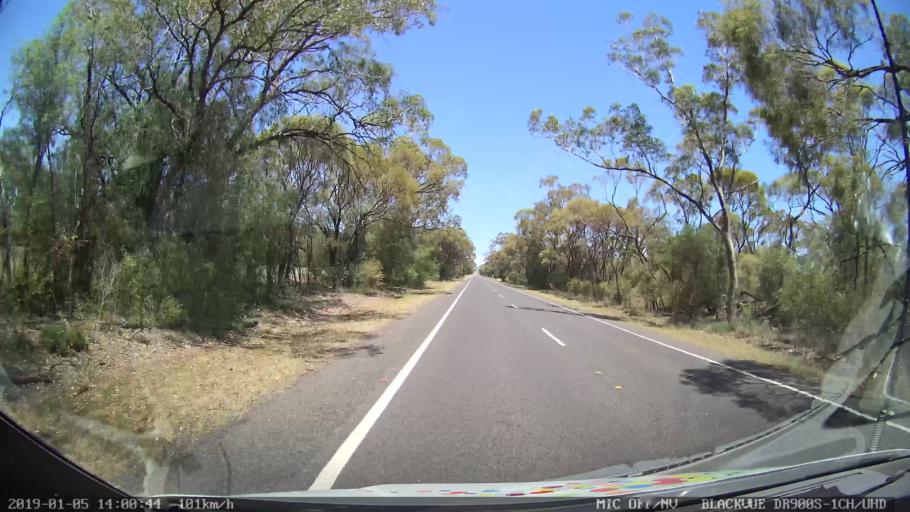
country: AU
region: New South Wales
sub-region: Gunnedah
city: Gunnedah
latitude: -31.1626
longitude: 150.3160
